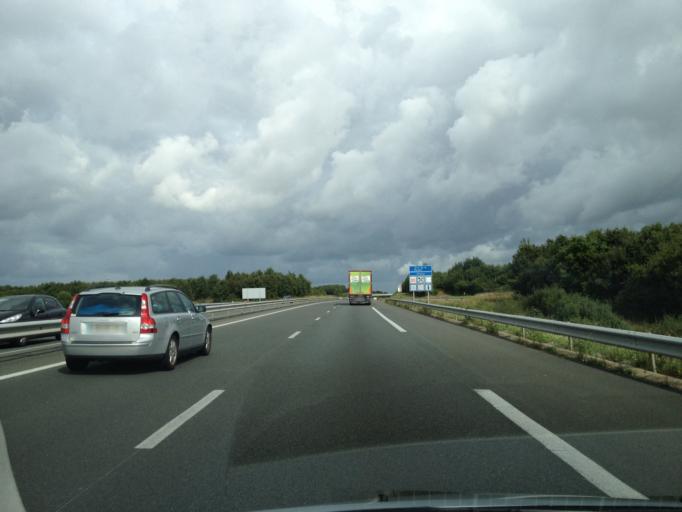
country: FR
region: Pays de la Loire
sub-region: Departement de la Vendee
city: Sainte-Hermine
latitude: 46.5607
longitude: -1.1034
